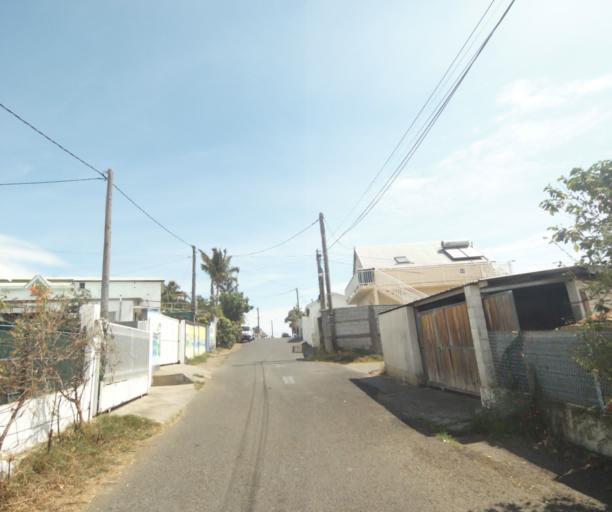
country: RE
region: Reunion
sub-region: Reunion
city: Saint-Paul
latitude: -21.0582
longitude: 55.2600
